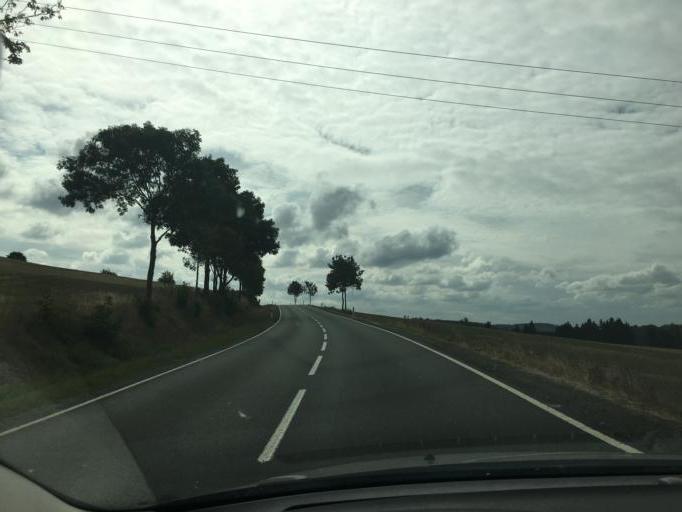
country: DE
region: Thuringia
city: Burgk
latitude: 50.5096
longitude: 11.7321
